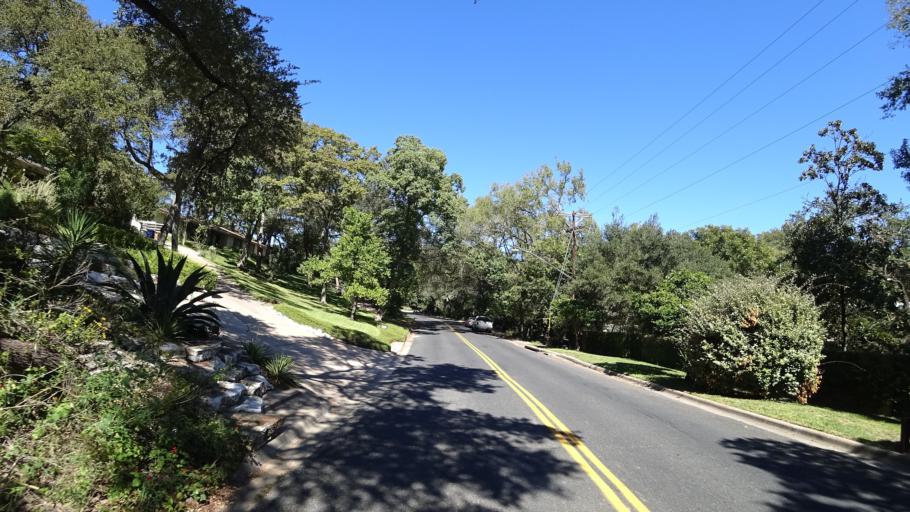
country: US
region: Texas
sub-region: Travis County
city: West Lake Hills
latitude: 30.3268
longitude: -97.7667
